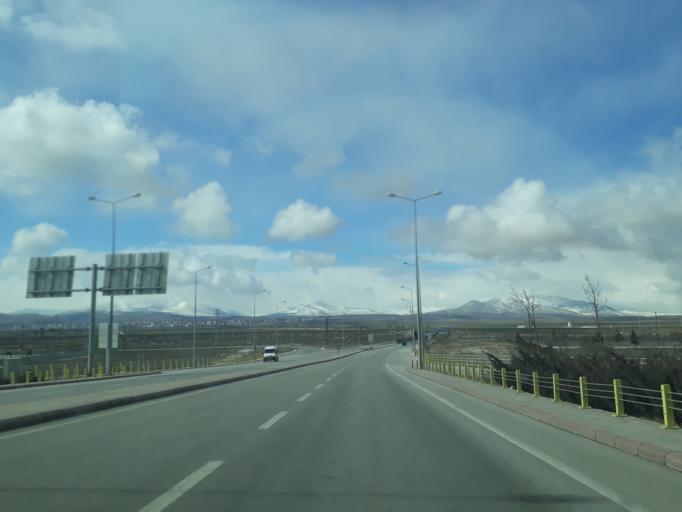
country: TR
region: Konya
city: Asagipinarbasi
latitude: 37.9914
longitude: 32.5937
